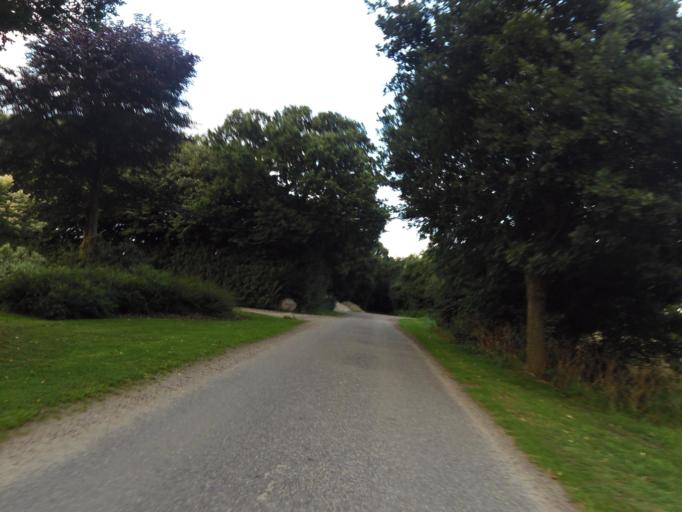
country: DK
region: South Denmark
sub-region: Esbjerg Kommune
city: Ribe
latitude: 55.2969
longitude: 8.7870
